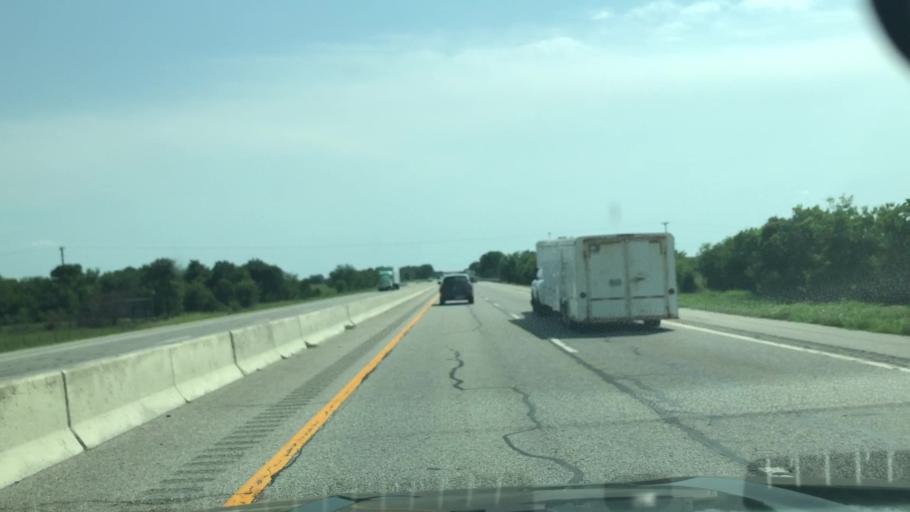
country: US
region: Oklahoma
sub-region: Ottawa County
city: Fairland
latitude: 36.7882
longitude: -94.8864
